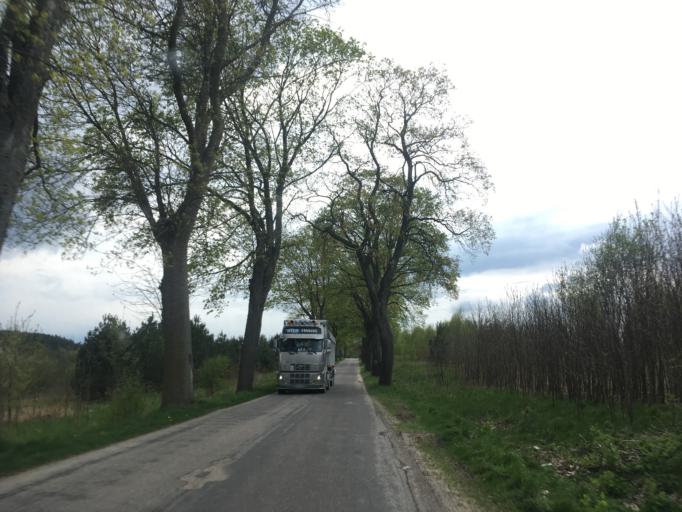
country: PL
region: Warmian-Masurian Voivodeship
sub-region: Powiat nidzicki
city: Kozlowo
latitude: 53.4123
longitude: 20.2690
